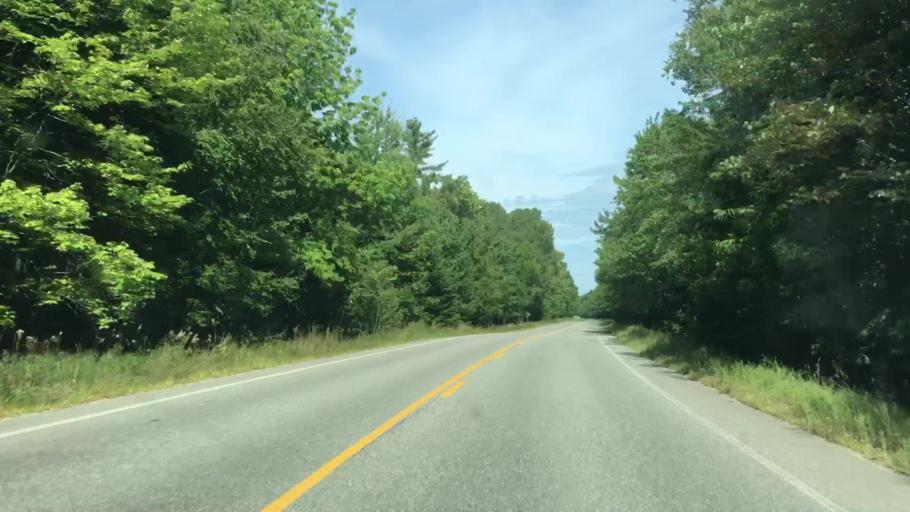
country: US
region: Maine
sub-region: Penobscot County
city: Lincoln
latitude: 45.3798
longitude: -68.5479
